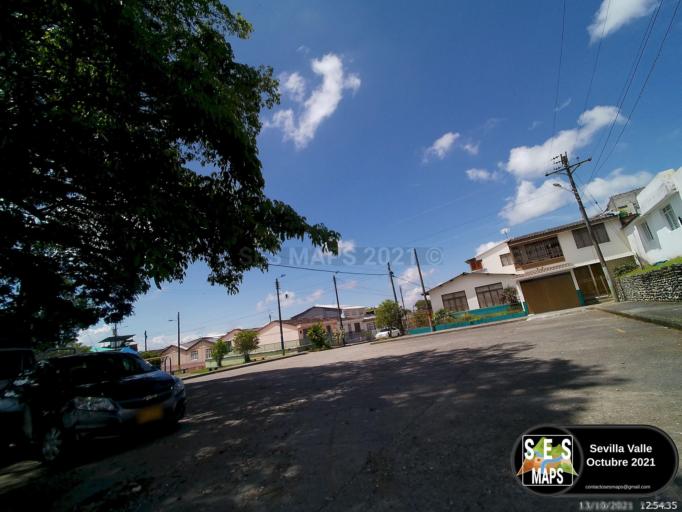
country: CO
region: Valle del Cauca
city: Sevilla
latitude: 4.2715
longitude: -75.9307
